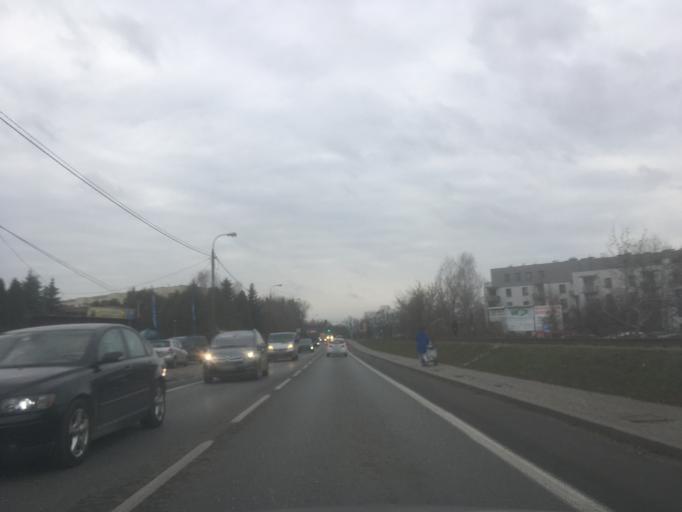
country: PL
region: Masovian Voivodeship
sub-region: Powiat piaseczynski
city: Piaseczno
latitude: 52.0668
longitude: 21.0215
